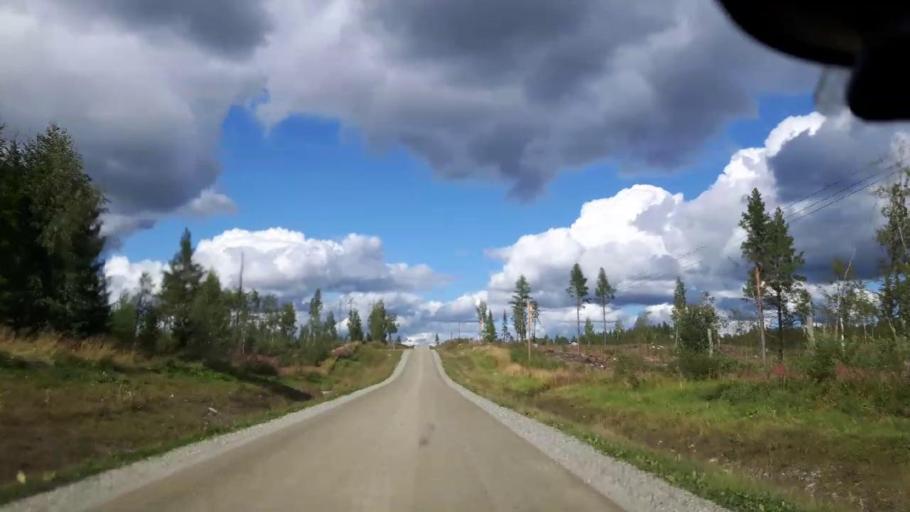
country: SE
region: Jaemtland
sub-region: Stroemsunds Kommun
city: Stroemsund
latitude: 63.3577
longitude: 15.5686
